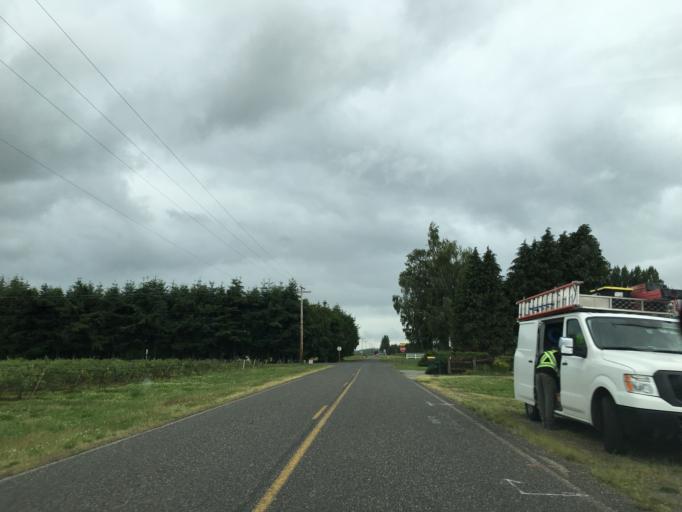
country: US
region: Washington
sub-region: Whatcom County
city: Lynden
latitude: 48.9786
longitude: -122.4058
